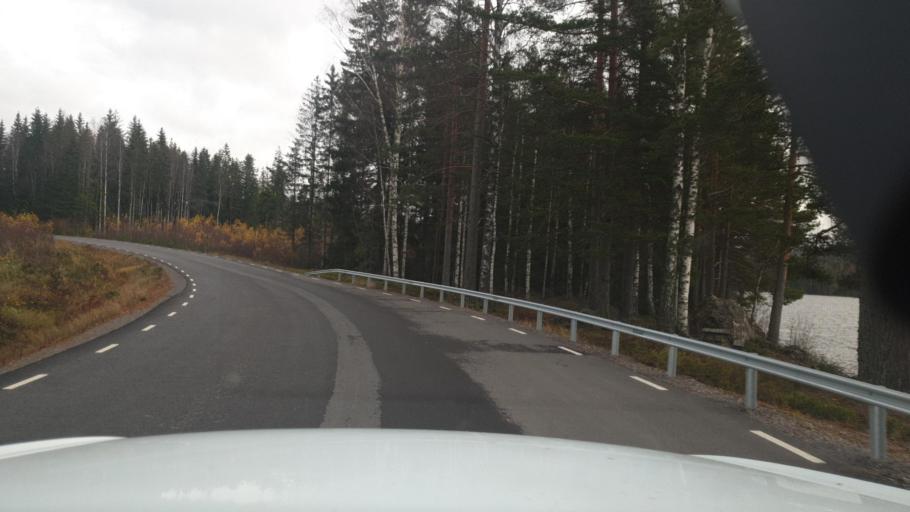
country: SE
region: Vaermland
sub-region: Torsby Kommun
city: Torsby
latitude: 59.9803
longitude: 12.8018
